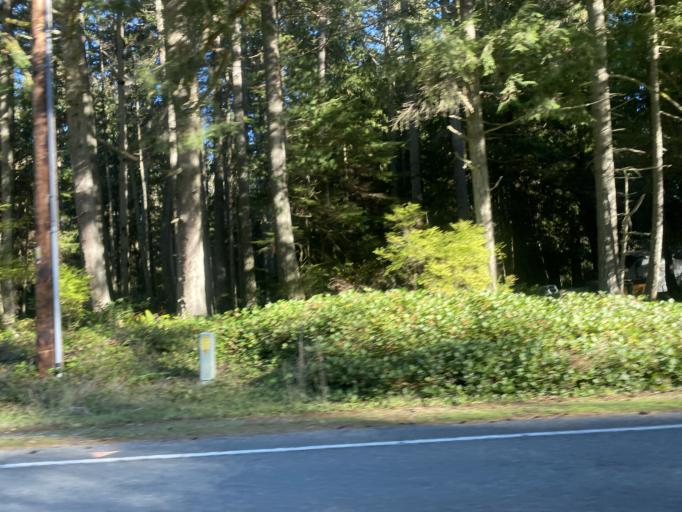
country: US
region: Washington
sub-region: Island County
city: Langley
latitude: 48.0192
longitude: -122.4273
